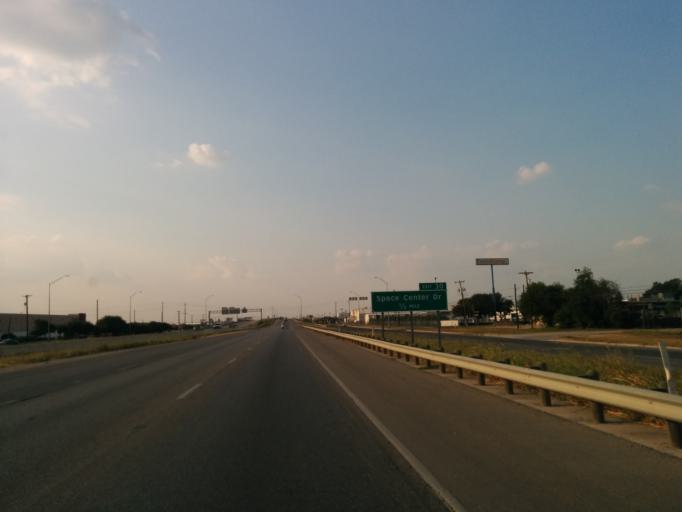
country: US
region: Texas
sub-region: Bexar County
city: Kirby
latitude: 29.4550
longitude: -98.4041
